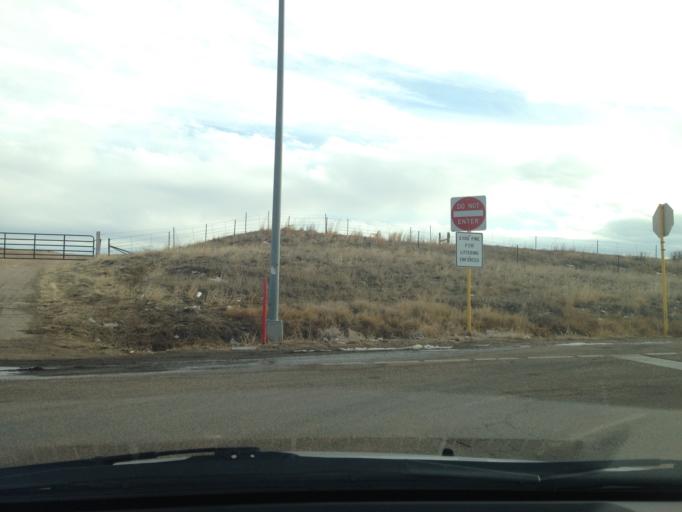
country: US
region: Colorado
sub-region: Weld County
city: Keenesburg
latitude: 40.2156
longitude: -104.2150
